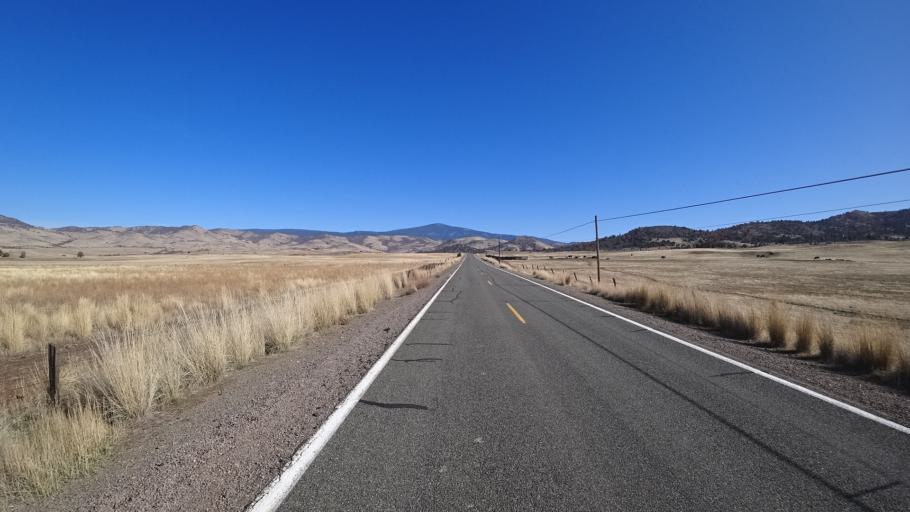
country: US
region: California
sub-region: Siskiyou County
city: Montague
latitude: 41.8044
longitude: -122.4075
